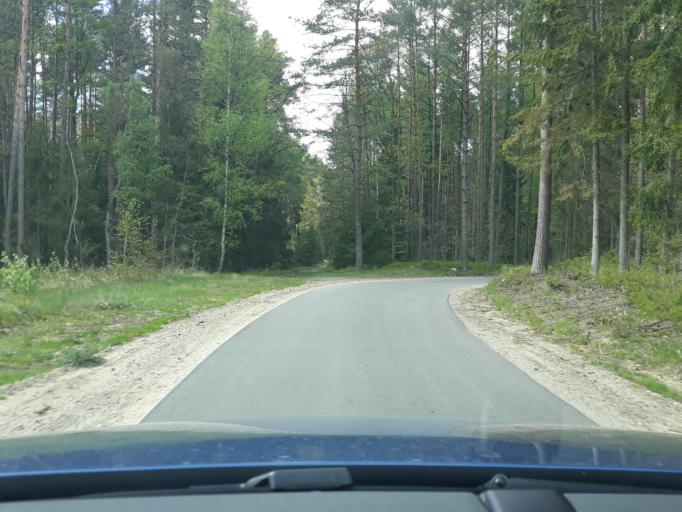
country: PL
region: Pomeranian Voivodeship
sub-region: Powiat czluchowski
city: Czluchow
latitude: 53.7360
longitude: 17.3424
